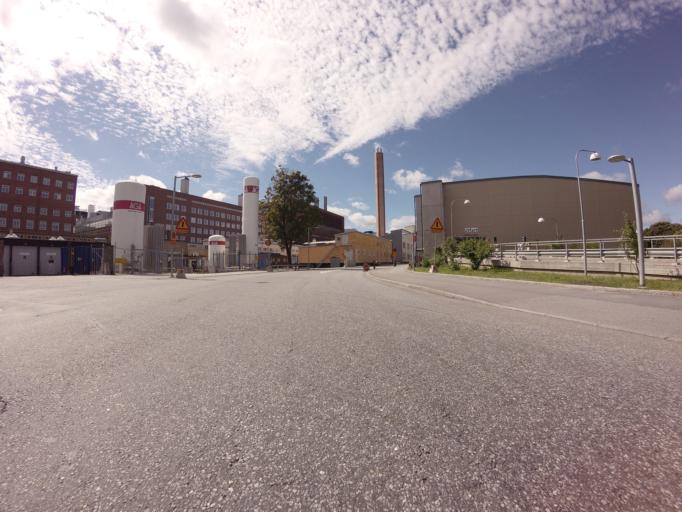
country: SE
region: Stockholm
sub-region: Norrtalje Kommun
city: Bergshamra
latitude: 59.3523
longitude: 18.0296
